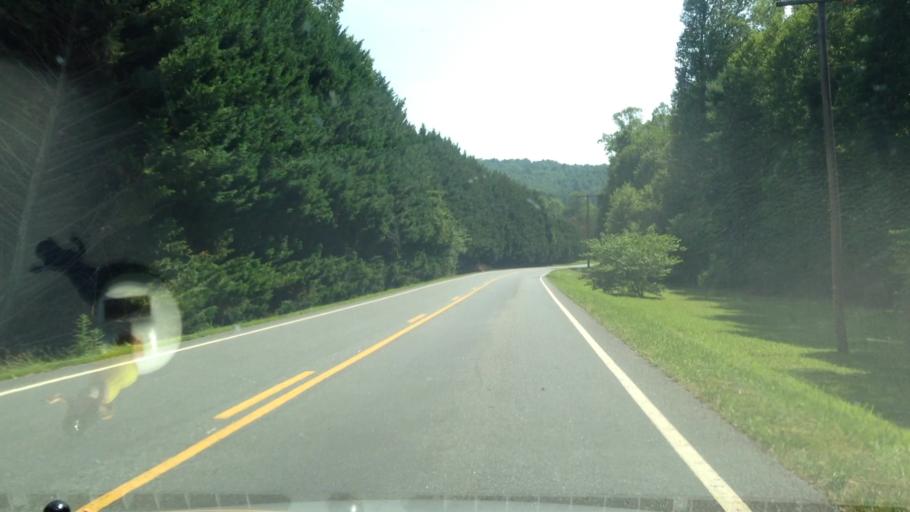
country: US
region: North Carolina
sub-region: Surry County
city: Flat Rock
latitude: 36.5762
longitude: -80.4470
